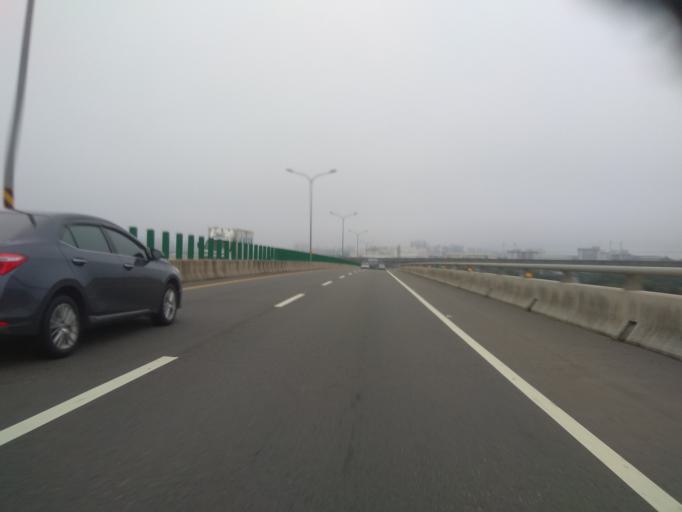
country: TW
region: Taiwan
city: Taoyuan City
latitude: 24.9570
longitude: 121.1473
